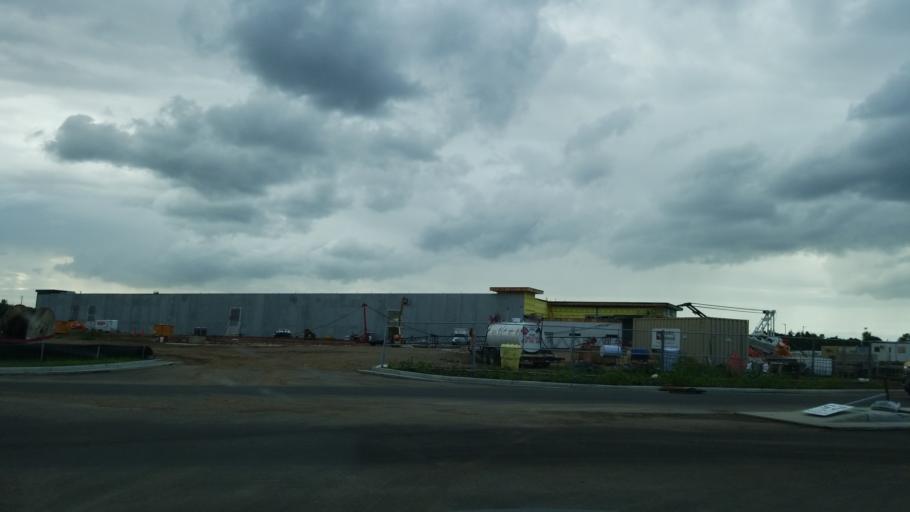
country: US
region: Minnesota
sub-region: Washington County
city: Lakeland
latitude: 44.9452
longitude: -92.7266
